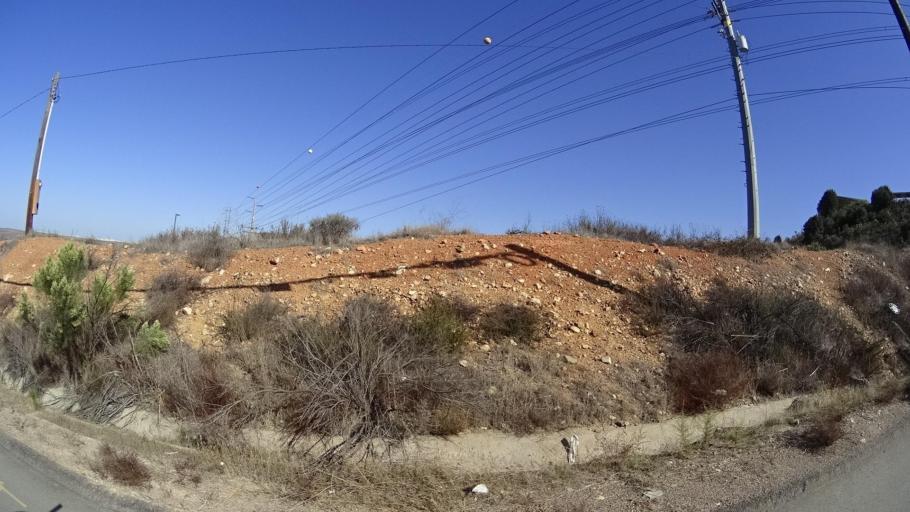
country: MX
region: Baja California
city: Tijuana
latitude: 32.5914
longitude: -116.9258
